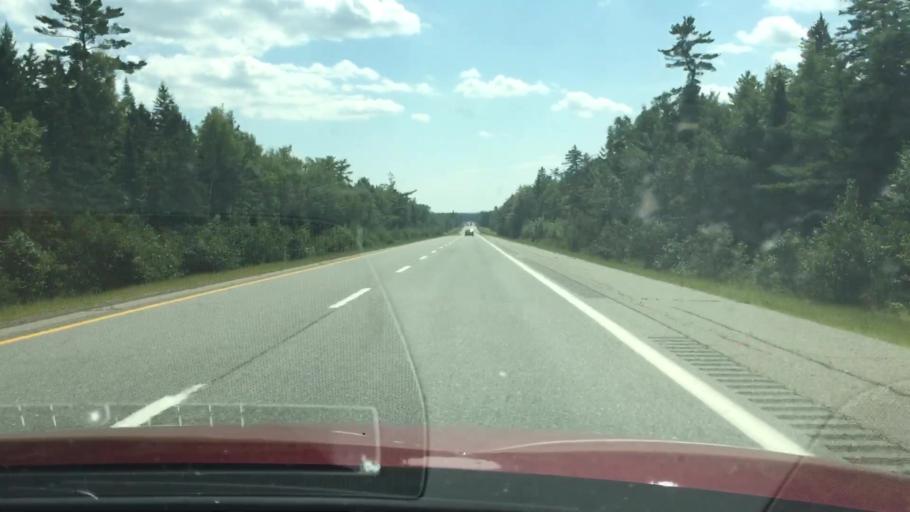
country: US
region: Maine
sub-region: Penobscot County
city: Greenbush
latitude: 45.0333
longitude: -68.6934
